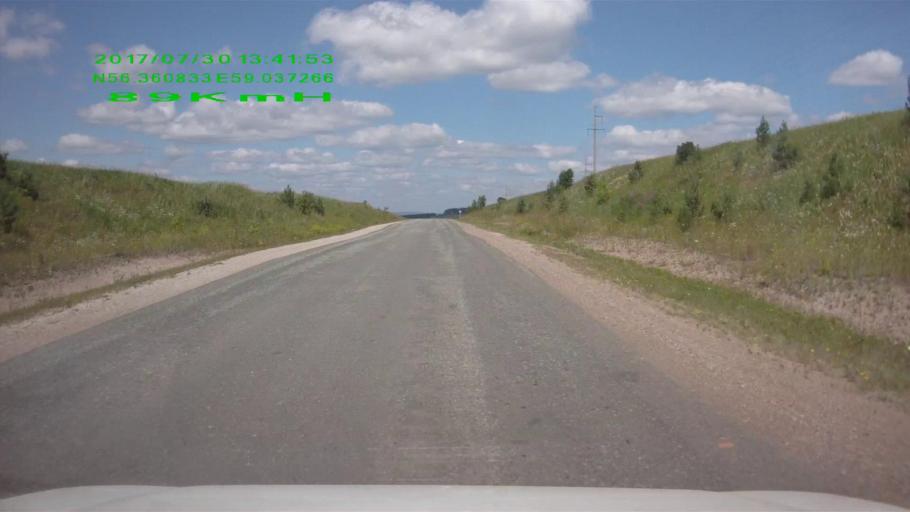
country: RU
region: Sverdlovsk
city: Mikhaylovsk
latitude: 56.3614
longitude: 59.0373
